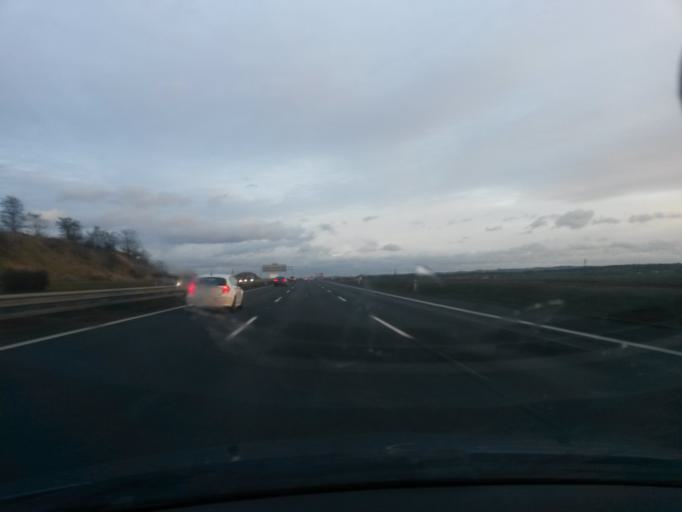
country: CZ
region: Central Bohemia
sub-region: Okres Praha-Zapad
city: Pruhonice
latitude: 50.0166
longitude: 14.5236
